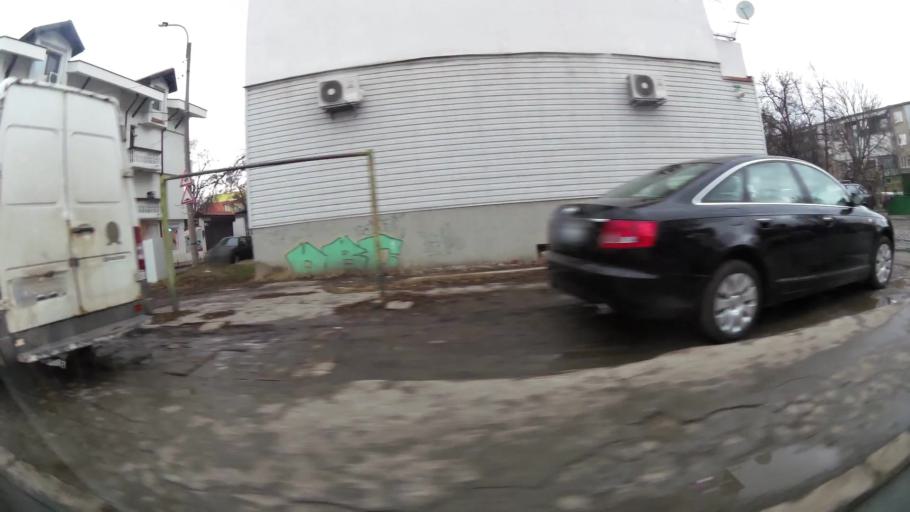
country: BG
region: Sofia-Capital
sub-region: Stolichna Obshtina
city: Sofia
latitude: 42.7354
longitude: 23.3043
